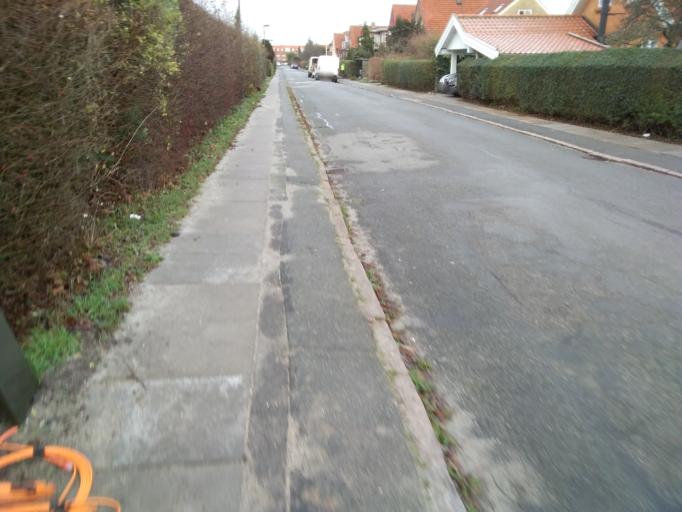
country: DK
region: Capital Region
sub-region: Tarnby Kommune
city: Tarnby
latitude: 55.6410
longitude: 12.6186
